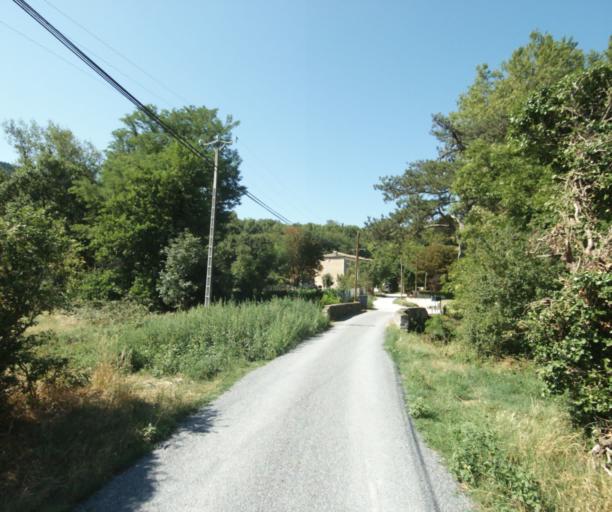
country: FR
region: Midi-Pyrenees
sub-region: Departement du Tarn
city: Soreze
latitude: 43.4444
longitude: 2.0565
